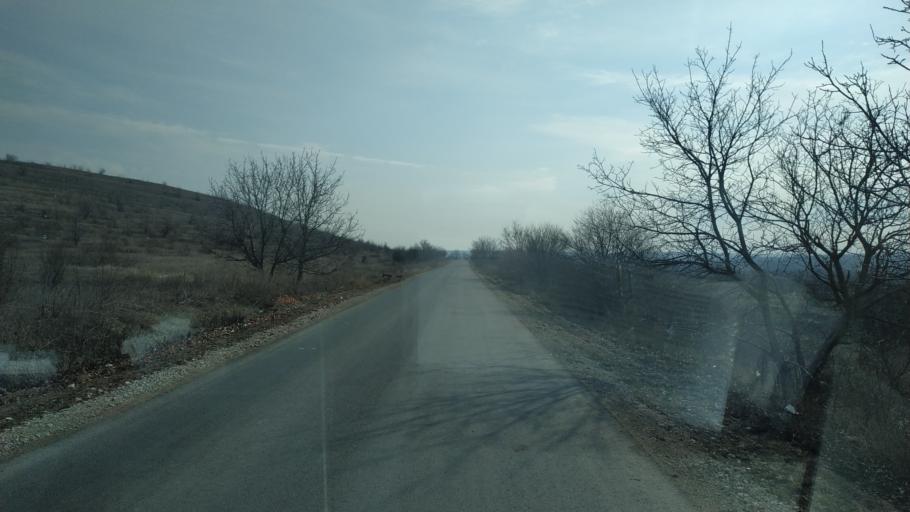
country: MD
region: Chisinau
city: Singera
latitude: 46.9221
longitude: 29.0940
